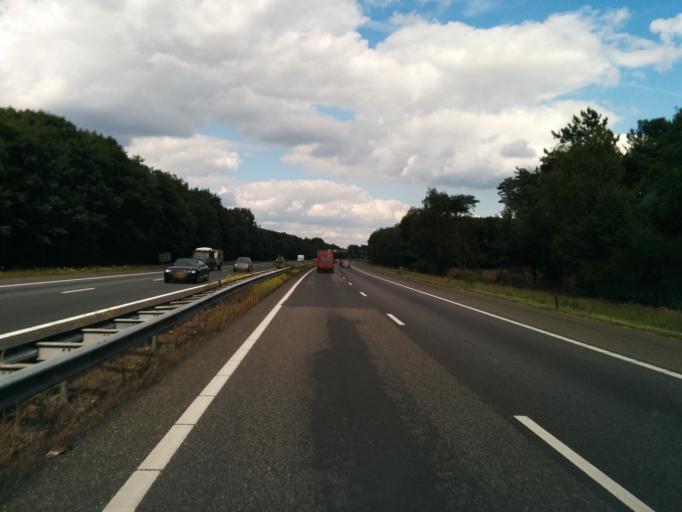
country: NL
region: North Brabant
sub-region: Gemeente Geldrop-Mierlo
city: Geldrop
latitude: 51.4172
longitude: 5.5933
